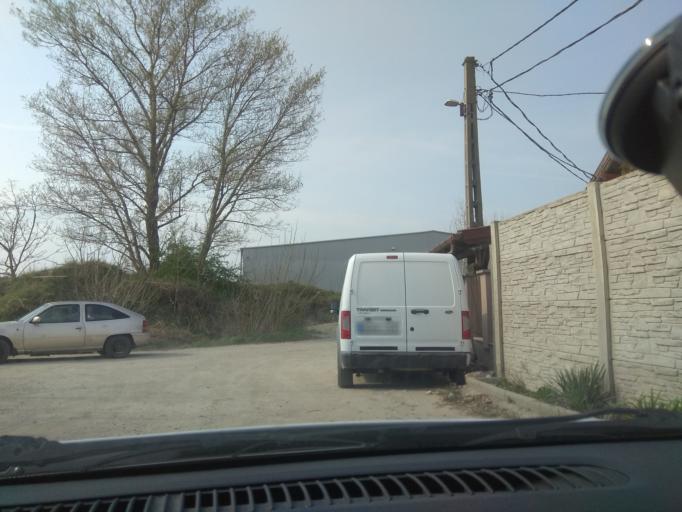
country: HU
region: Pest
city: Szigetszentmiklos
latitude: 47.3737
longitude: 19.0543
